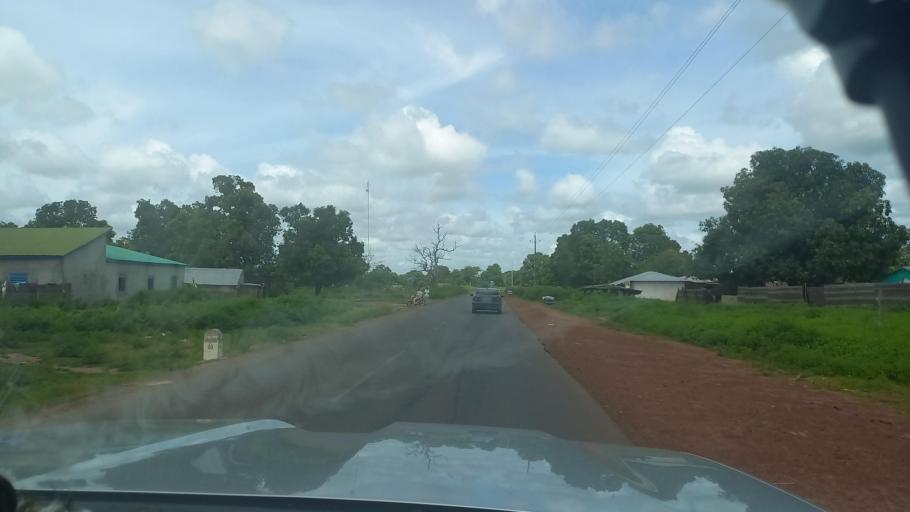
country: GM
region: Lower River
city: Kaiaf
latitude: 13.2043
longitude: -15.5494
